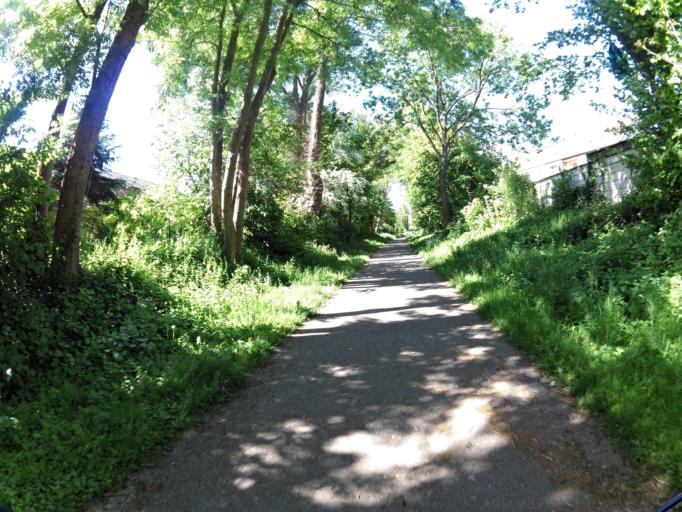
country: DE
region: North Rhine-Westphalia
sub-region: Regierungsbezirk Koln
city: Aldenhoven
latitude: 50.8955
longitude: 6.2959
